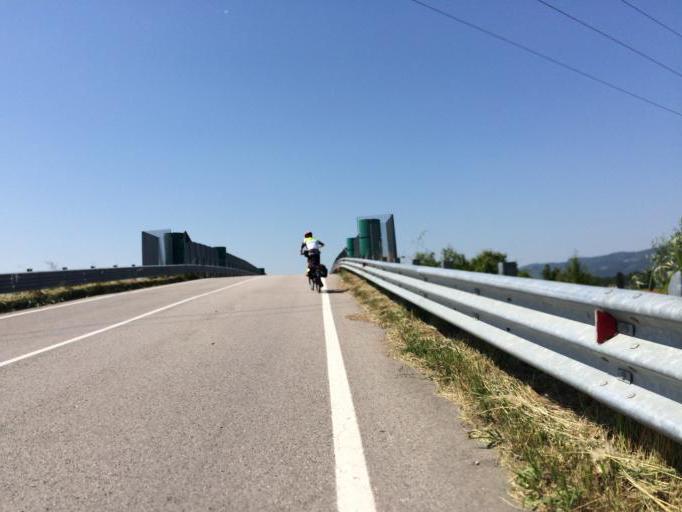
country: IT
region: Veneto
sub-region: Provincia di Vicenza
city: Villaganzerla
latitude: 45.4447
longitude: 11.6332
